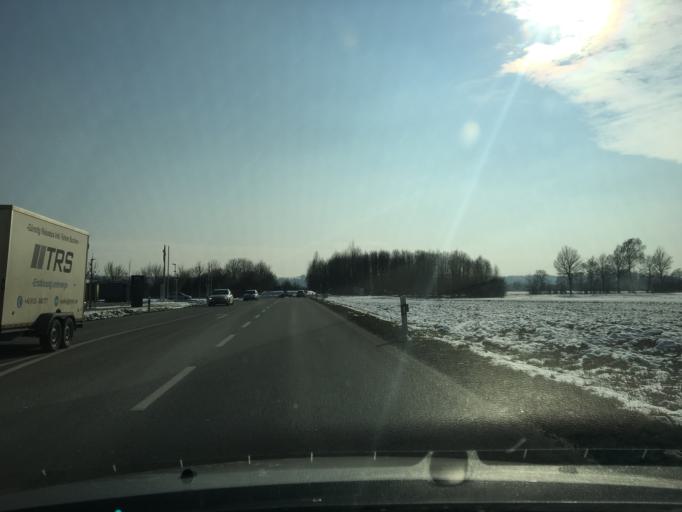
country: DE
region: Bavaria
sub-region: Lower Bavaria
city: Gottfrieding
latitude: 48.6519
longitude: 12.5246
